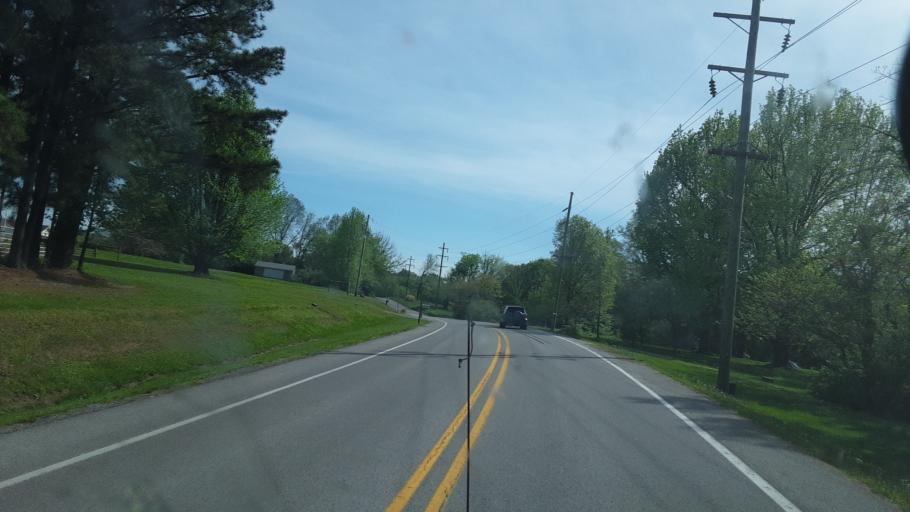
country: US
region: Illinois
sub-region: Jackson County
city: Carbondale
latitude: 37.6805
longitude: -89.2579
